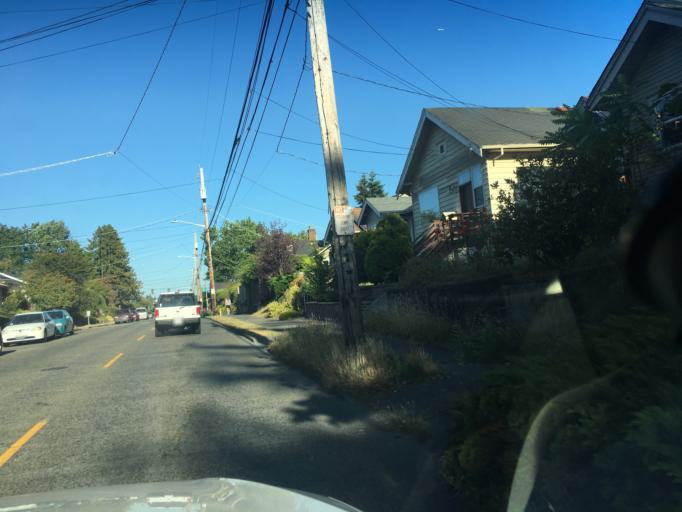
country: US
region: Washington
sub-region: King County
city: Shoreline
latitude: 47.6869
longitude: -122.3491
